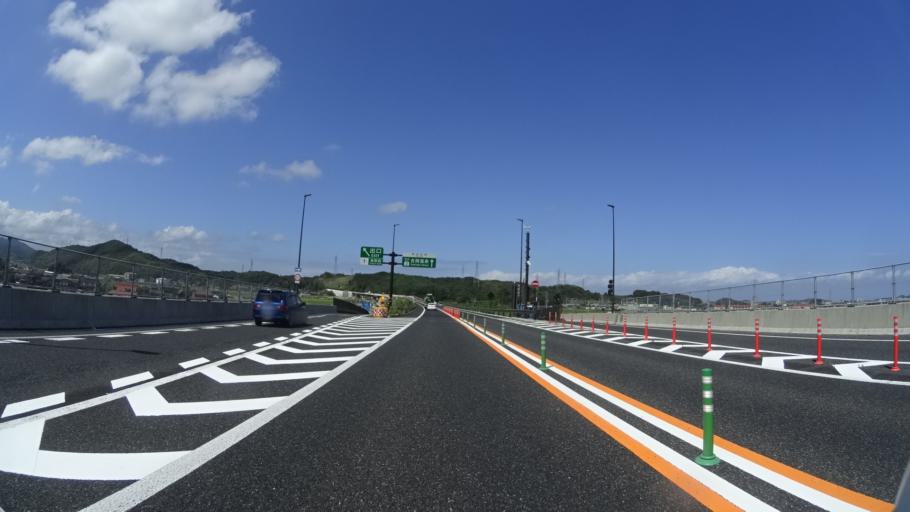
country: JP
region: Tottori
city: Tottori
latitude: 35.4921
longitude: 134.1934
